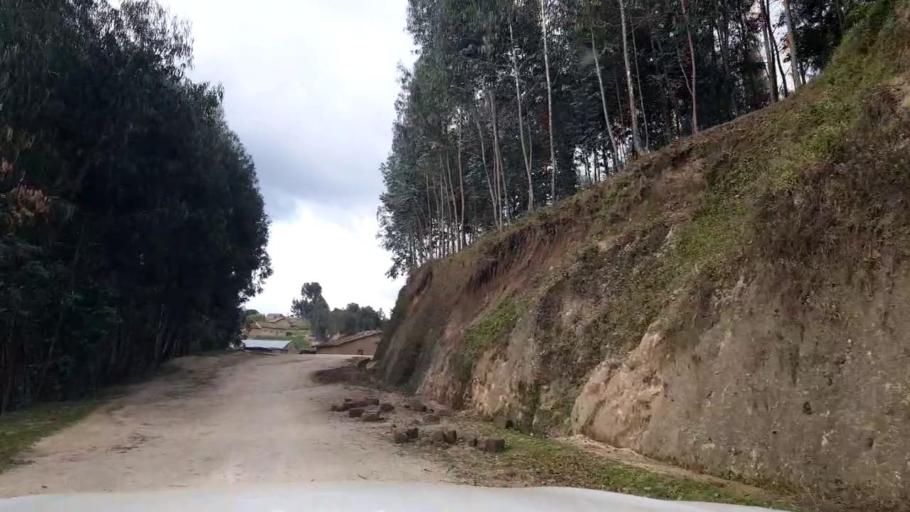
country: RW
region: Western Province
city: Kibuye
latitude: -1.8653
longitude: 29.5476
